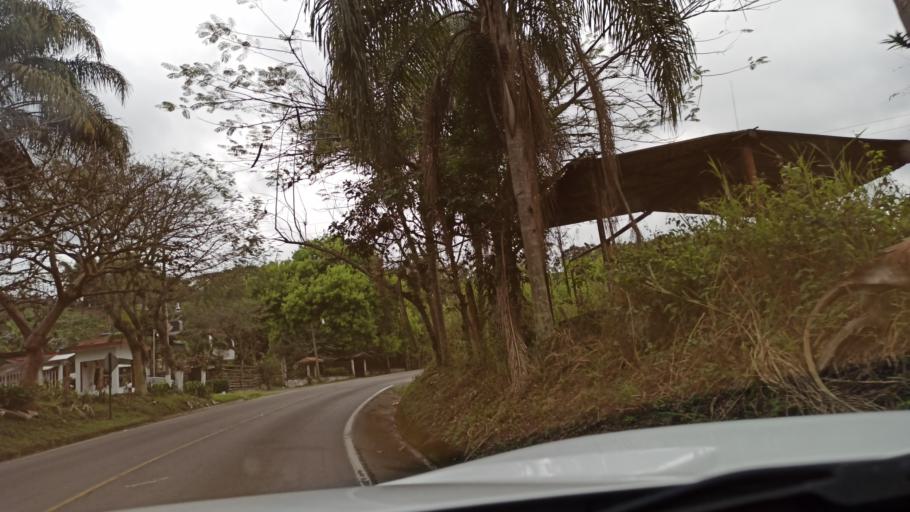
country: MX
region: Veracruz
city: Cuautlapan
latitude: 18.8905
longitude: -97.0111
